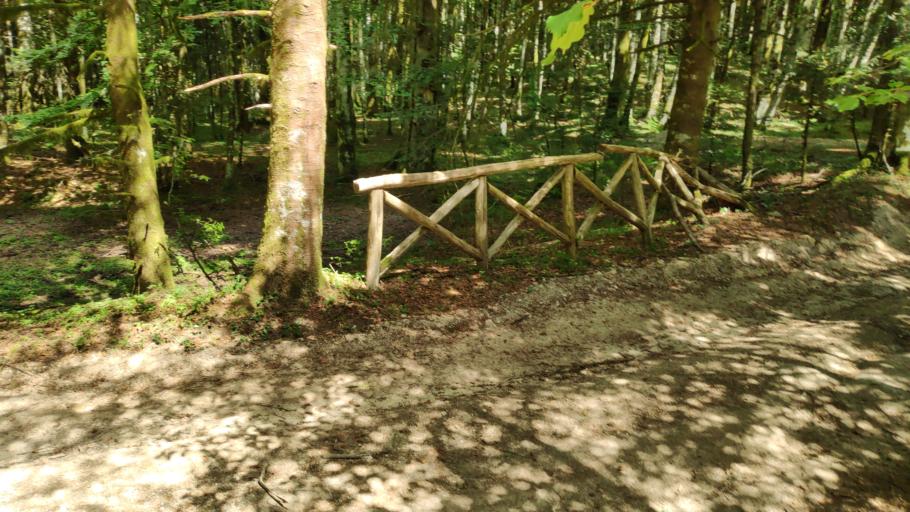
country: IT
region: Calabria
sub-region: Provincia di Vibo-Valentia
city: Mongiana
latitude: 38.5396
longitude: 16.3543
